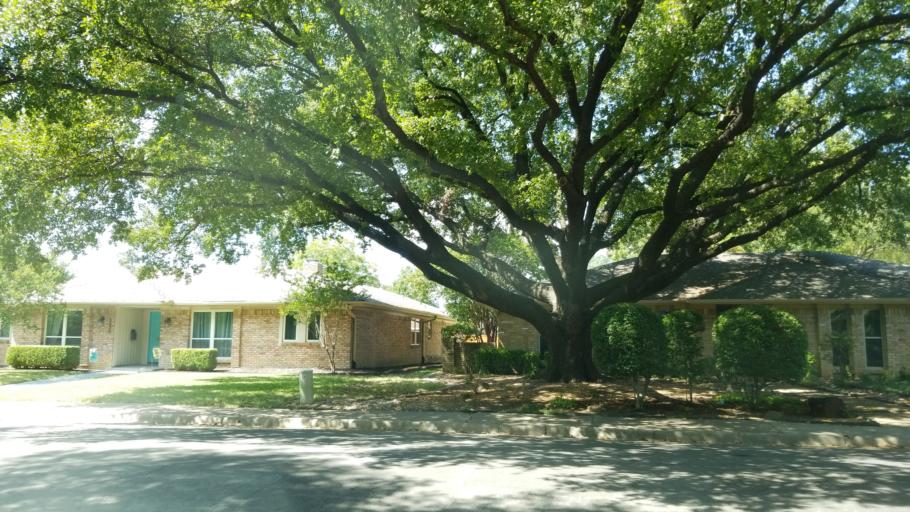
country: US
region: Texas
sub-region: Dallas County
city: Addison
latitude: 32.9655
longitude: -96.7840
